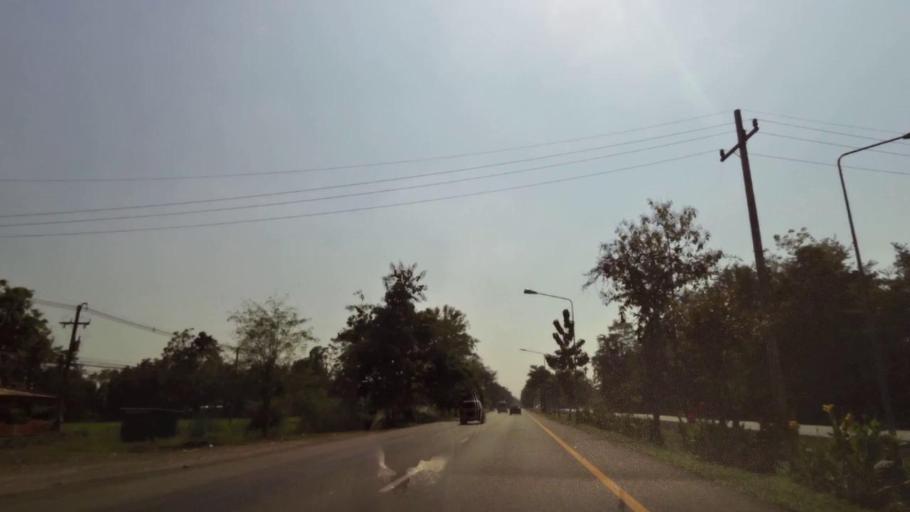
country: TH
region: Phichit
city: Bueng Na Rang
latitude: 16.0746
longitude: 100.1241
